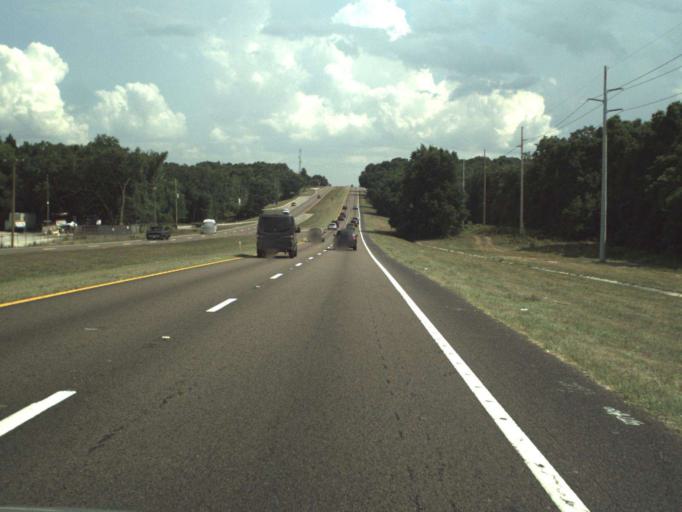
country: US
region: Florida
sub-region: Lake County
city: Mount Dora
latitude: 28.8061
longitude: -81.6257
